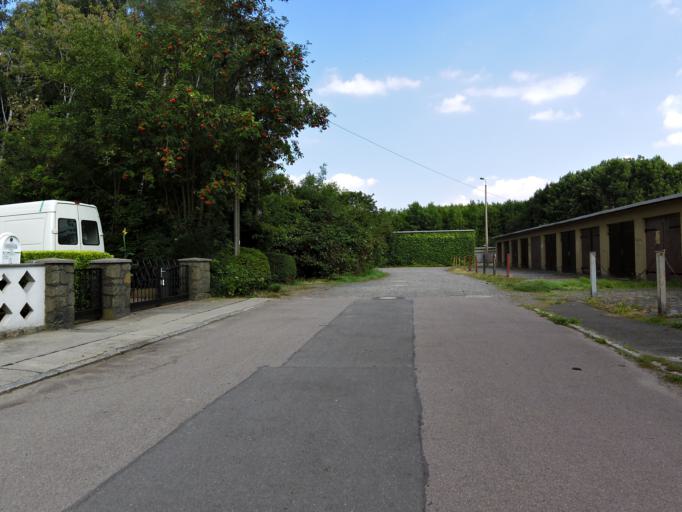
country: DE
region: Saxony
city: Leipzig
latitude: 51.3797
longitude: 12.3388
